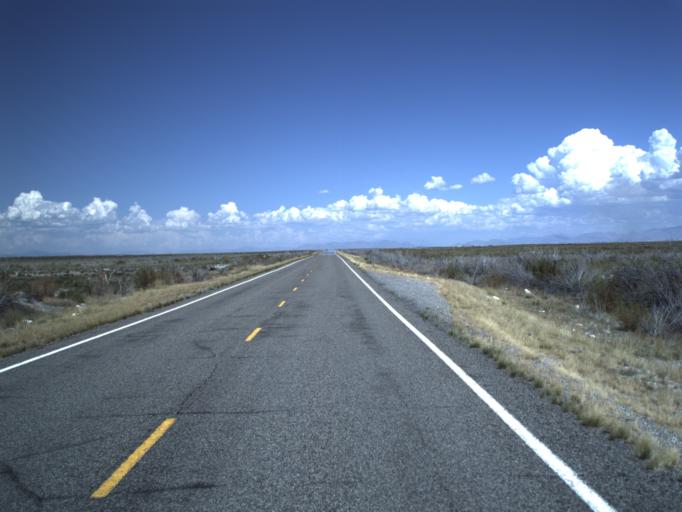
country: US
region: Utah
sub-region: Millard County
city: Delta
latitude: 39.2727
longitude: -112.8590
